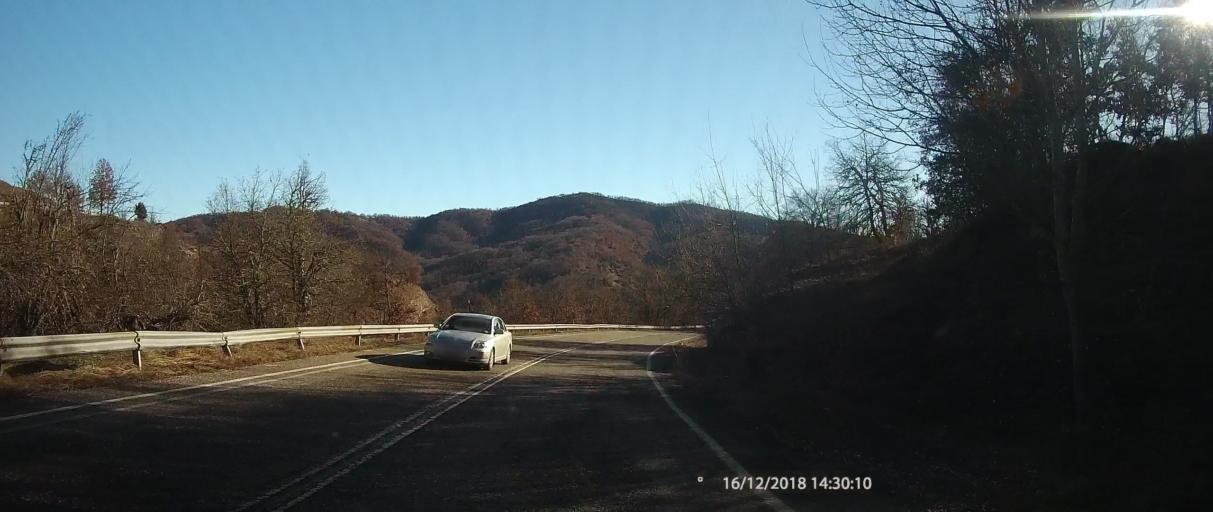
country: GR
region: West Macedonia
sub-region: Nomos Kozanis
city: Tsotili
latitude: 40.1999
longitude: 21.1896
